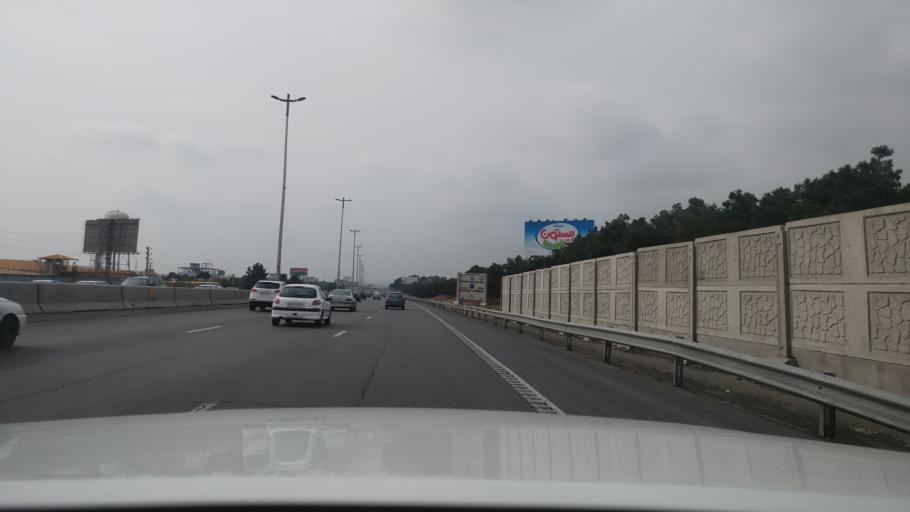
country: IR
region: Tehran
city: Shahr-e Qods
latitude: 35.7177
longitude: 51.2323
